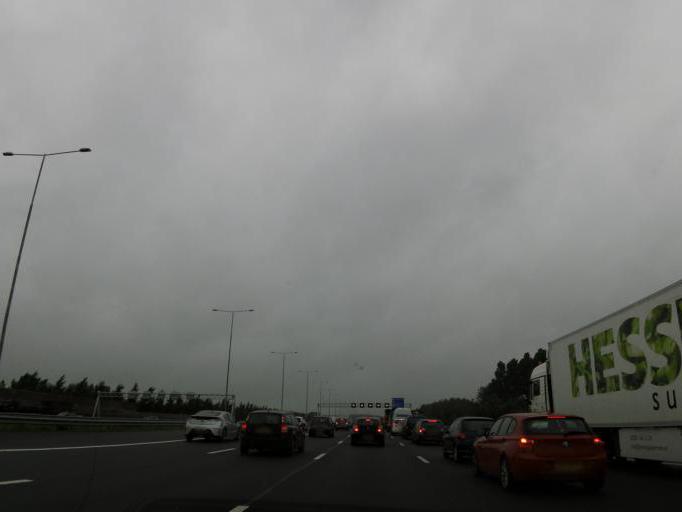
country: NL
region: North Holland
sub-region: Gemeente Amsterdam
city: Amsterdam-Zuidoost
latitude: 52.2526
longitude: 4.9685
